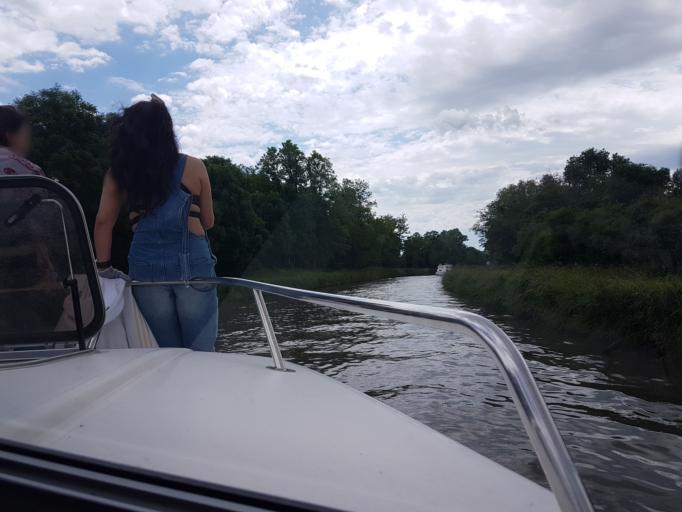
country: FR
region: Bourgogne
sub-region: Departement de la Nievre
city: Clamecy
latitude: 47.4901
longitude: 3.5243
